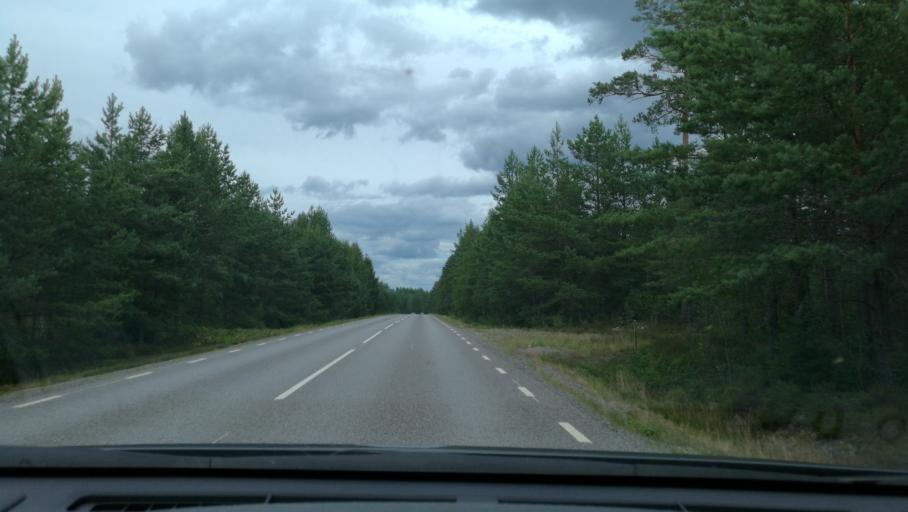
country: SE
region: OEstergoetland
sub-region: Norrkopings Kommun
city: Svartinge
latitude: 58.7468
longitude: 15.9740
